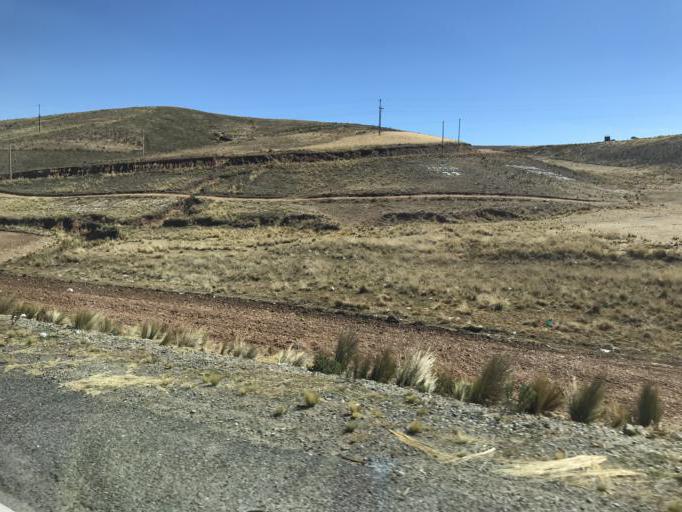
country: BO
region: La Paz
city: Tiahuanaco
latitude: -16.5782
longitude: -68.5366
